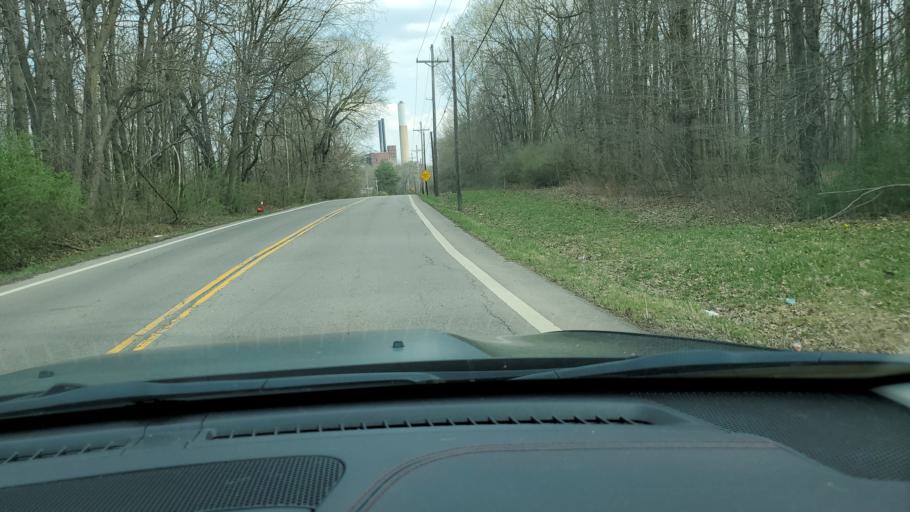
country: US
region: Ohio
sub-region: Trumbull County
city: Niles
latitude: 41.1687
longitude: -80.7585
